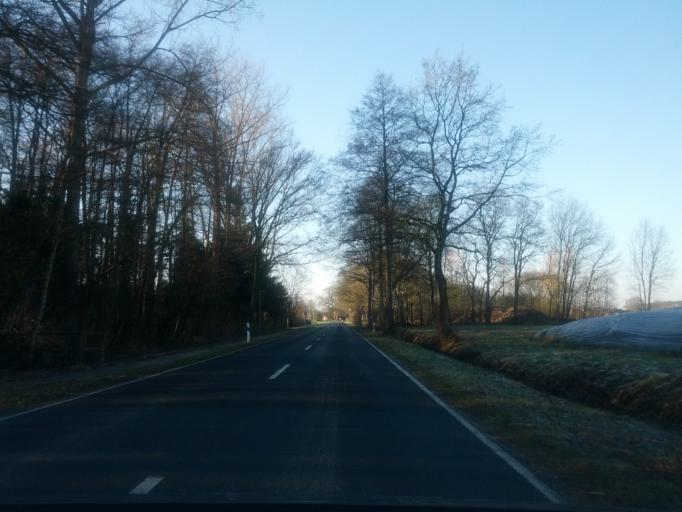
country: DE
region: Lower Saxony
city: Kalbe
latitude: 53.2869
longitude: 9.5506
